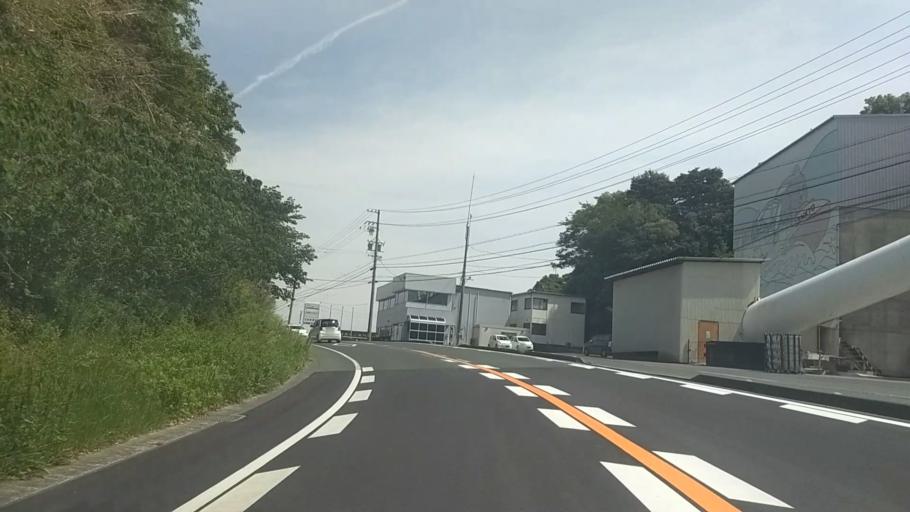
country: JP
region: Shizuoka
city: Kosai-shi
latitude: 34.7975
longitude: 137.5623
